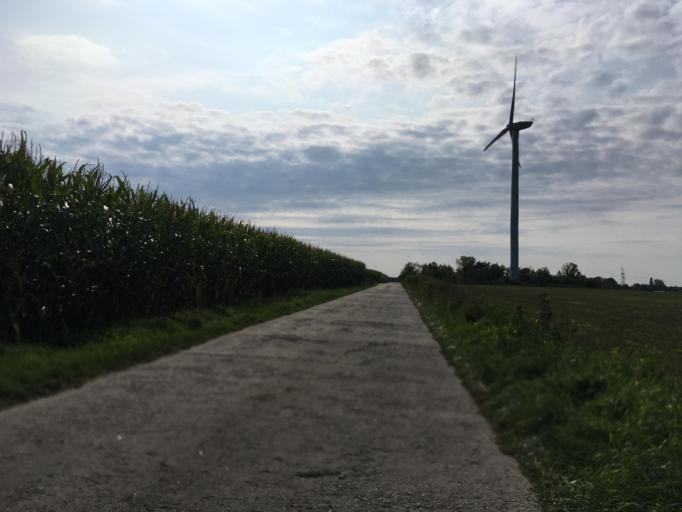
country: DE
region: Berlin
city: Blankenfelde
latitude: 52.6684
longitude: 13.4275
